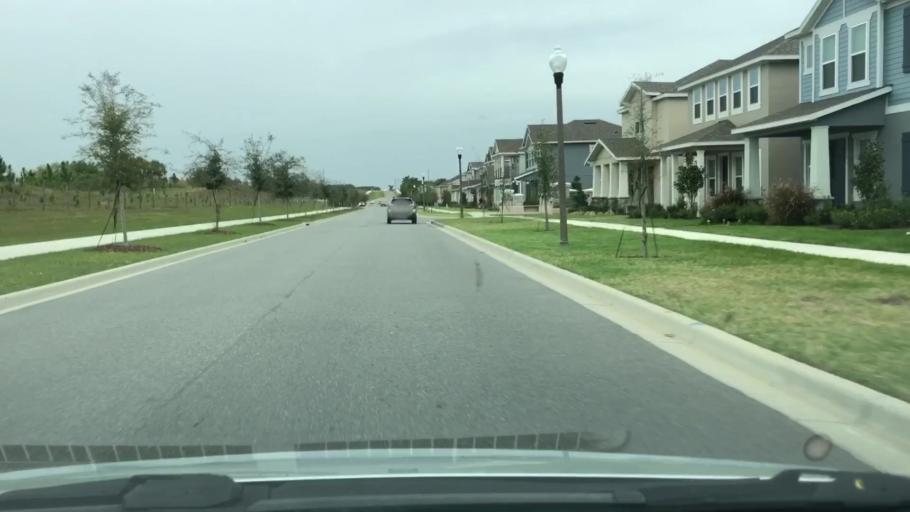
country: US
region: Florida
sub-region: Orange County
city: Lake Butler
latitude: 28.4372
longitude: -81.6237
